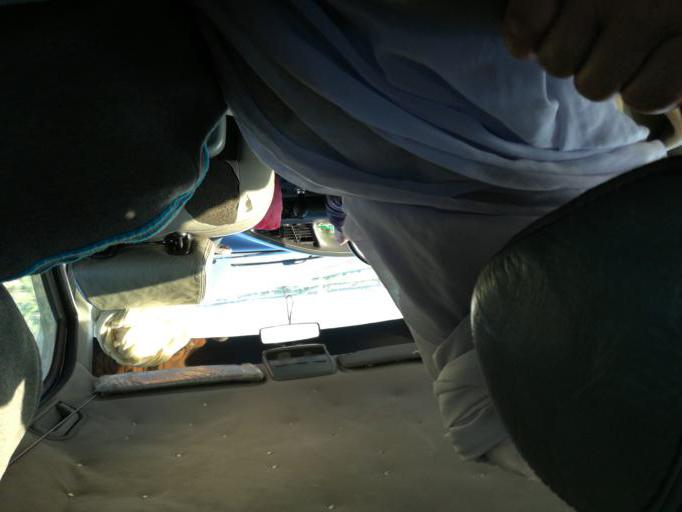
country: TN
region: Susah
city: Sidi Bou Ali
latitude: 36.0452
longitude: 10.3301
